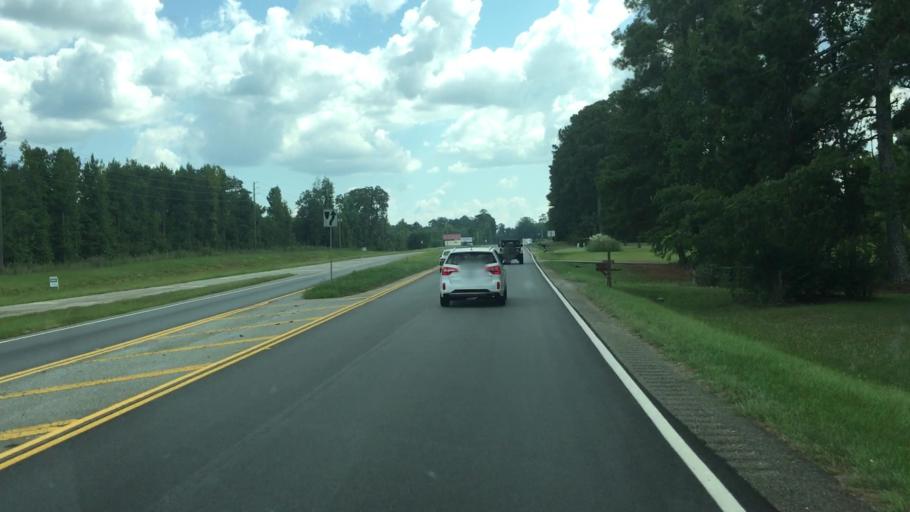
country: US
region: Georgia
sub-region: Putnam County
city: Eatonton
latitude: 33.3525
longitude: -83.3909
